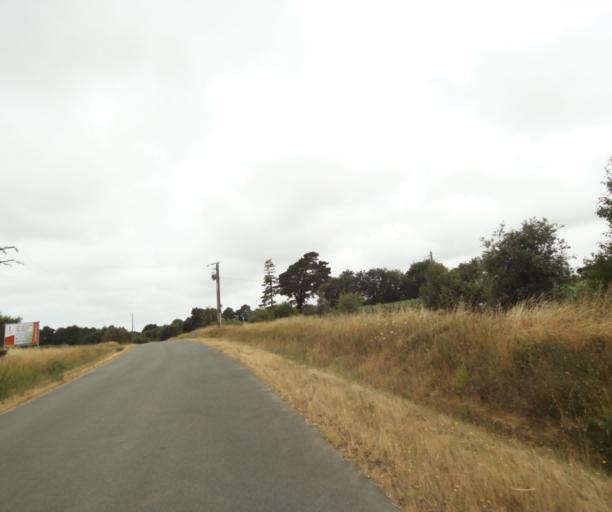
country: FR
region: Pays de la Loire
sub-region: Departement de la Vendee
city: Chateau-d'Olonne
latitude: 46.4971
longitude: -1.7057
